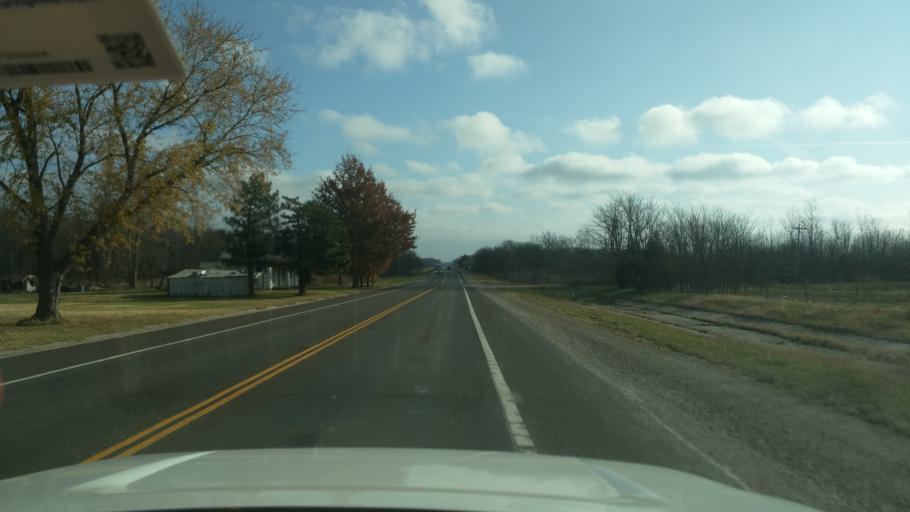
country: US
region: Kansas
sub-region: Montgomery County
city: Caney
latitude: 37.0679
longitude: -96.0129
